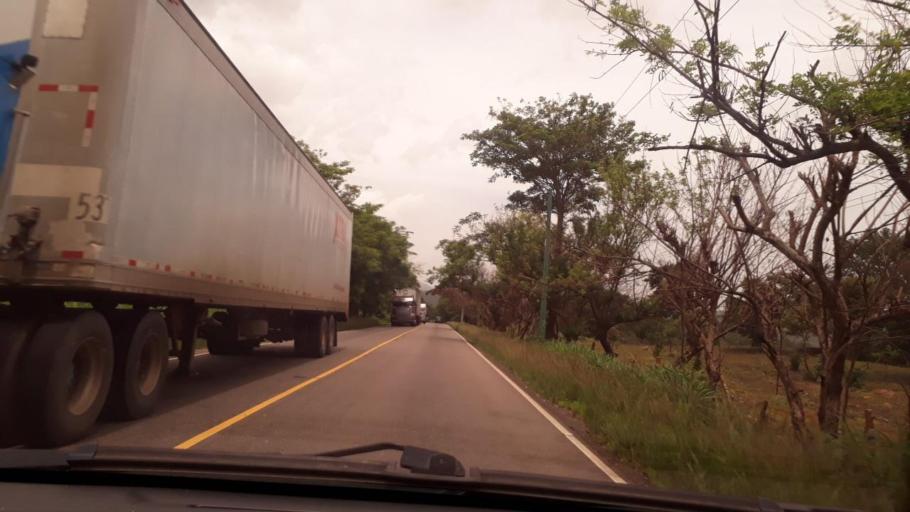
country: GT
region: Chiquimula
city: Quezaltepeque
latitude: 14.5840
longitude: -89.4555
